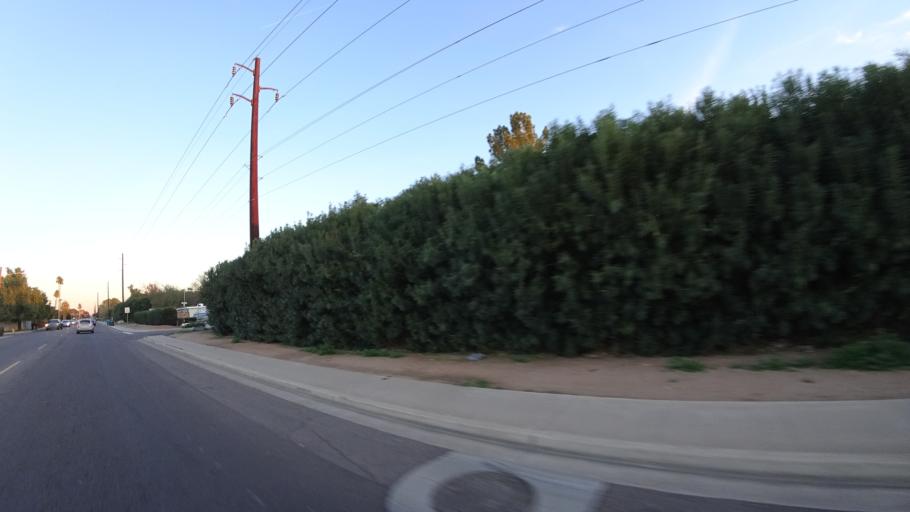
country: US
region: Arizona
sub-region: Maricopa County
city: Phoenix
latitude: 33.4731
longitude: -112.0013
